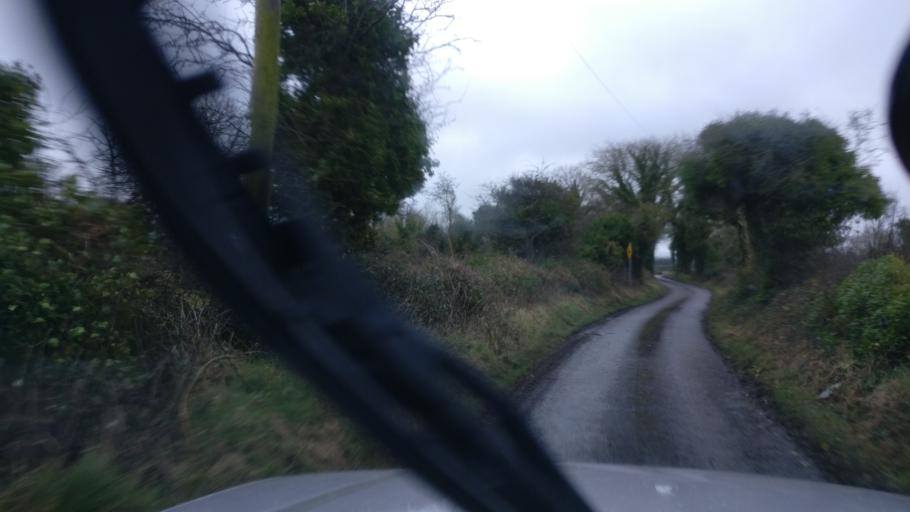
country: IE
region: Connaught
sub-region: County Galway
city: Loughrea
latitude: 53.2005
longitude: -8.6654
